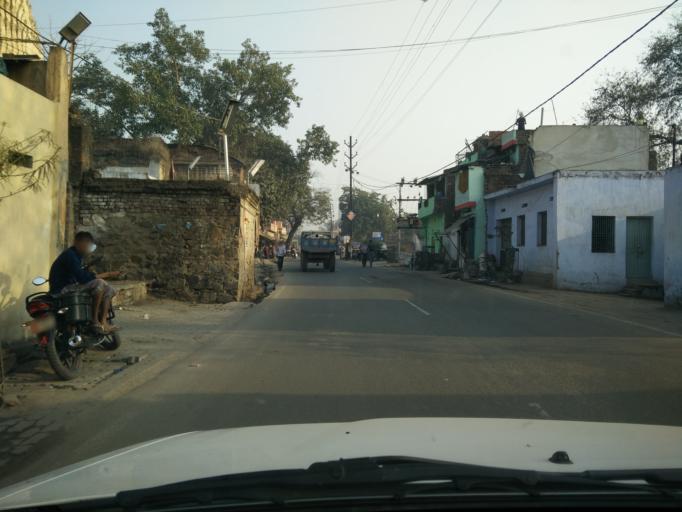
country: IN
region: Bihar
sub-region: Gaya
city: Gaya
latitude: 24.8116
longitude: 85.0154
